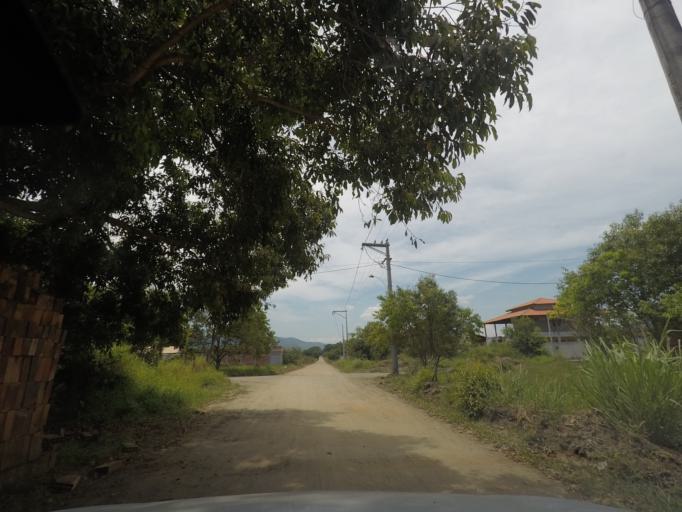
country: BR
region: Rio de Janeiro
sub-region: Marica
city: Marica
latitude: -22.9546
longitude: -42.9456
